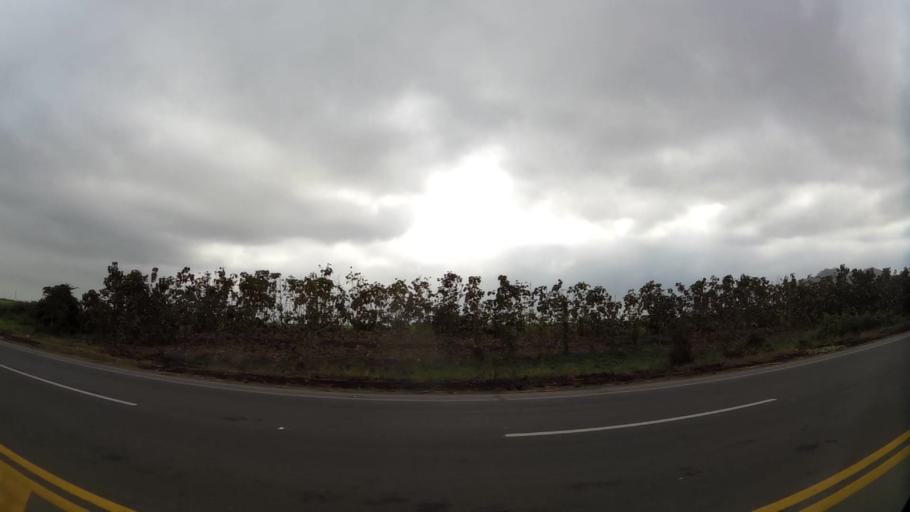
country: EC
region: Guayas
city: Coronel Marcelino Mariduena
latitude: -2.3652
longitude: -79.6328
